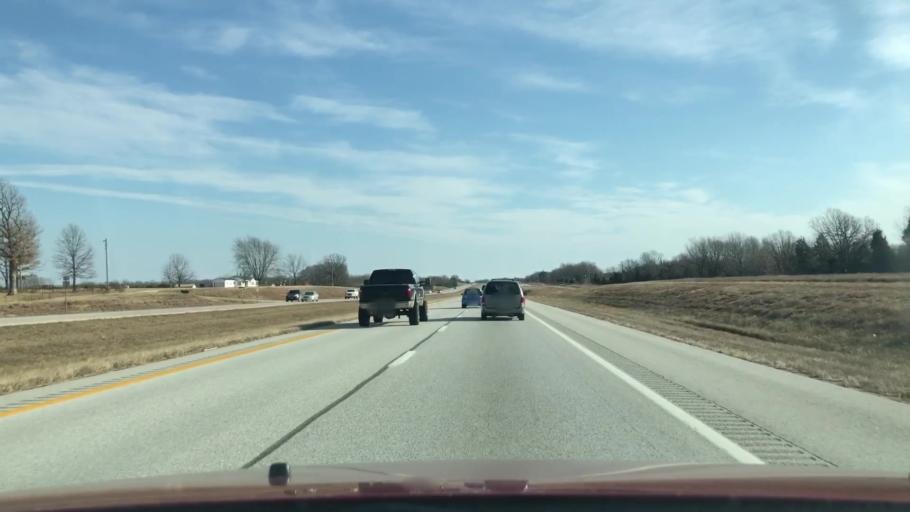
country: US
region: Missouri
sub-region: Webster County
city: Rogersville
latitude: 37.1595
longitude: -92.9161
